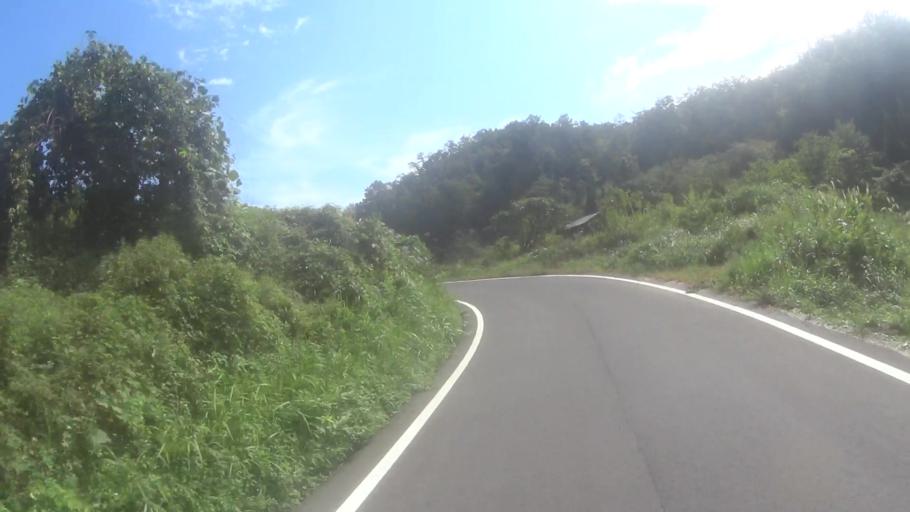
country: JP
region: Kyoto
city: Miyazu
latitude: 35.6161
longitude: 135.1267
